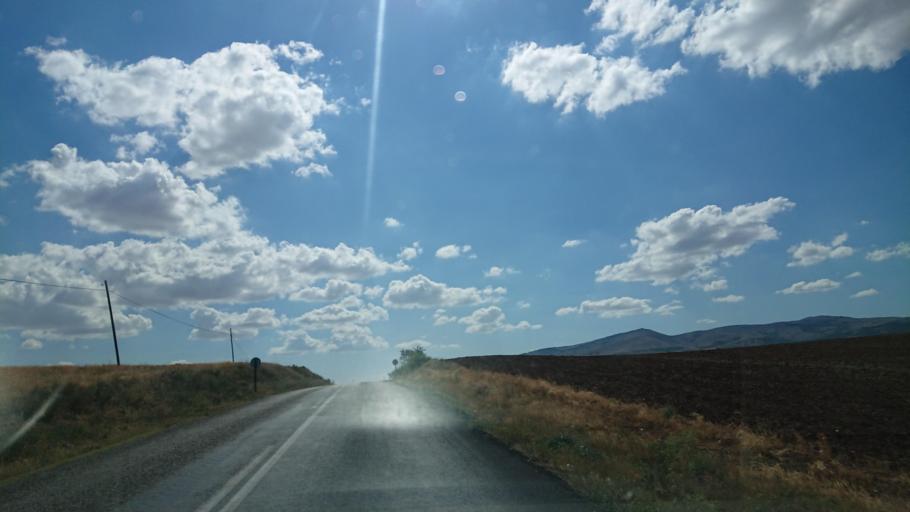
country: TR
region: Kirsehir
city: Kirsehir
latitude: 39.1517
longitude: 34.1060
